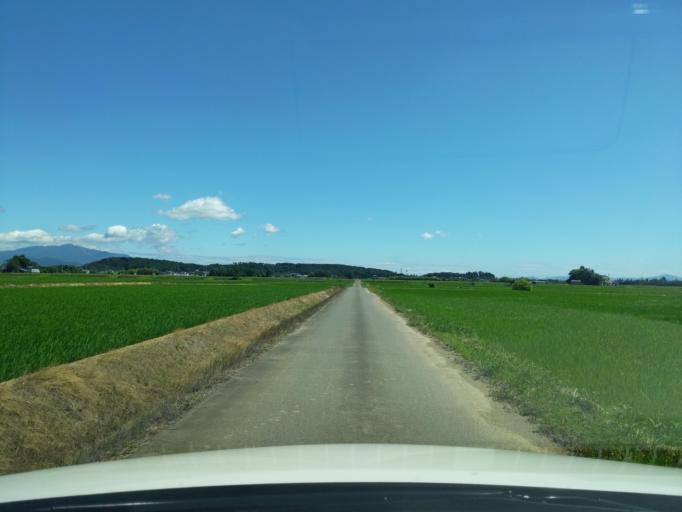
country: JP
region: Fukushima
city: Koriyama
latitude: 37.3796
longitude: 140.2999
